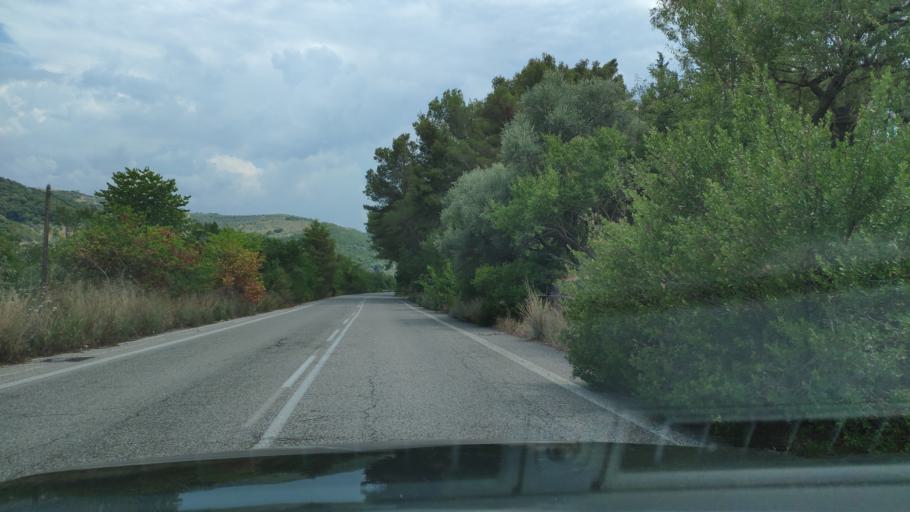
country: GR
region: West Greece
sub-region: Nomos Aitolias kai Akarnanias
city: Krikellos
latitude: 38.9942
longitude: 21.1545
